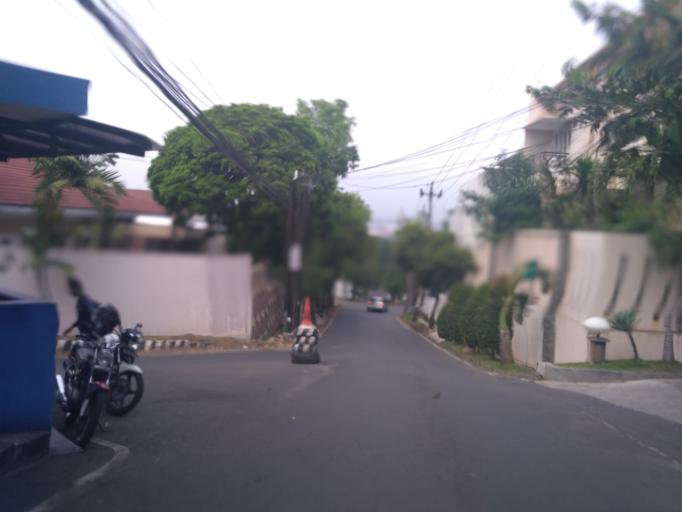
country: ID
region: Central Java
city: Semarang
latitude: -7.0455
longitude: 110.4262
